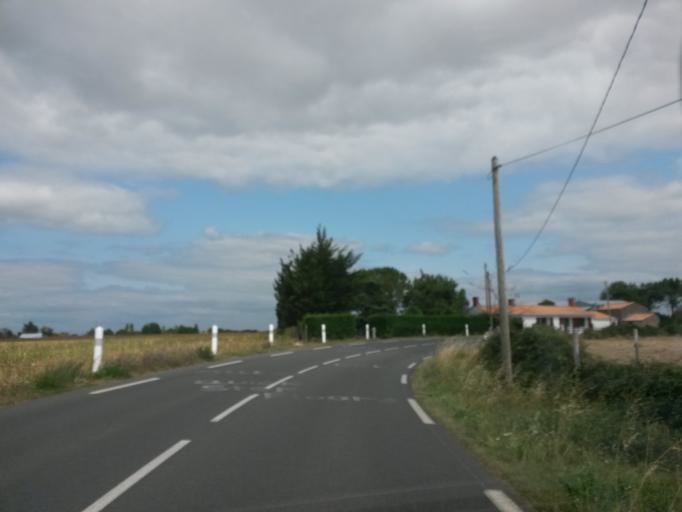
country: FR
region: Pays de la Loire
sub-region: Departement de la Vendee
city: Longeville-sur-Mer
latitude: 46.4237
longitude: -1.5165
